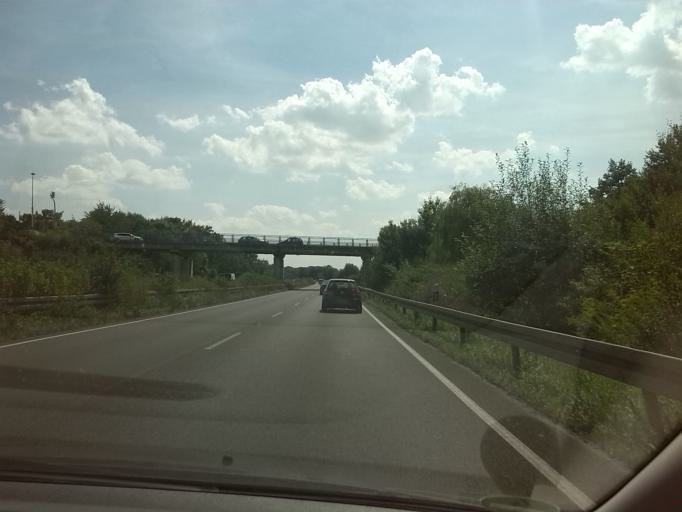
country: DE
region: Saxony
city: Markkleeberg
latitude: 51.2738
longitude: 12.3826
